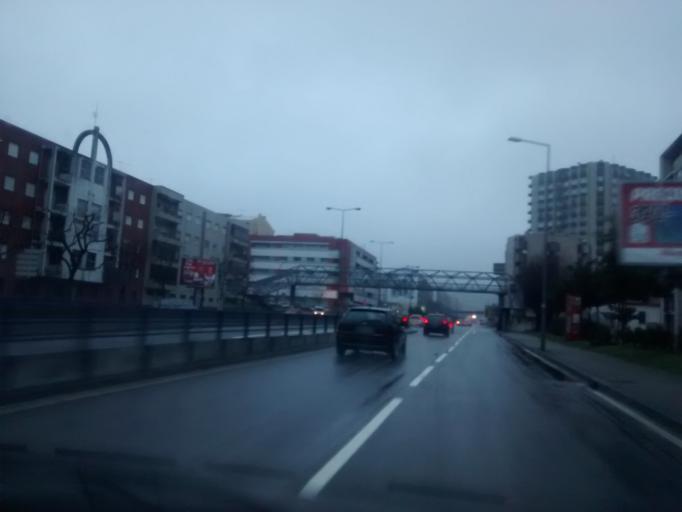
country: PT
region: Braga
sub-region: Braga
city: Braga
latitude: 41.5538
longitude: -8.4068
